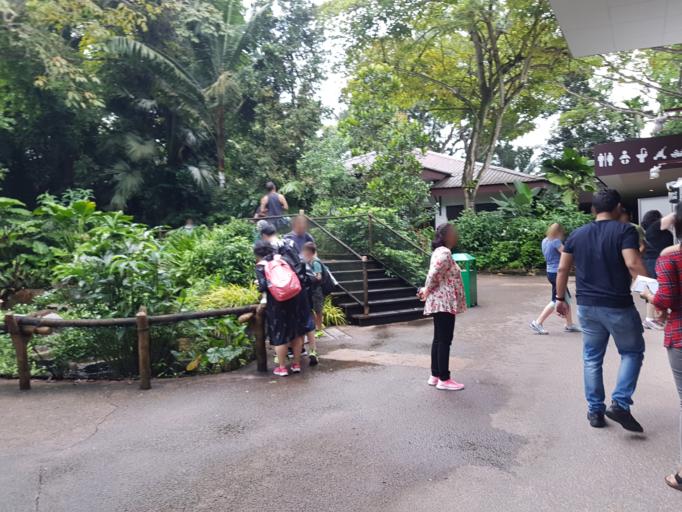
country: MY
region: Johor
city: Johor Bahru
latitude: 1.4050
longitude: 103.7907
